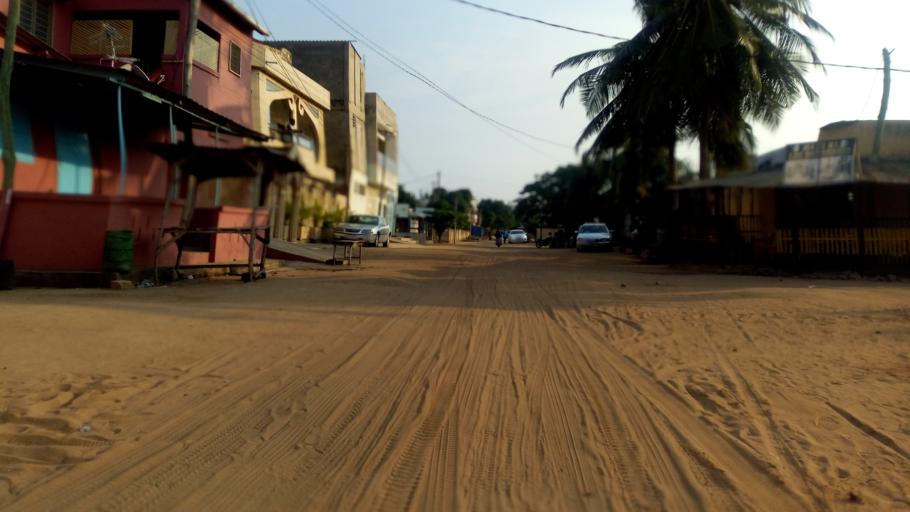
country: TG
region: Maritime
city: Lome
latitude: 6.1933
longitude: 1.1797
